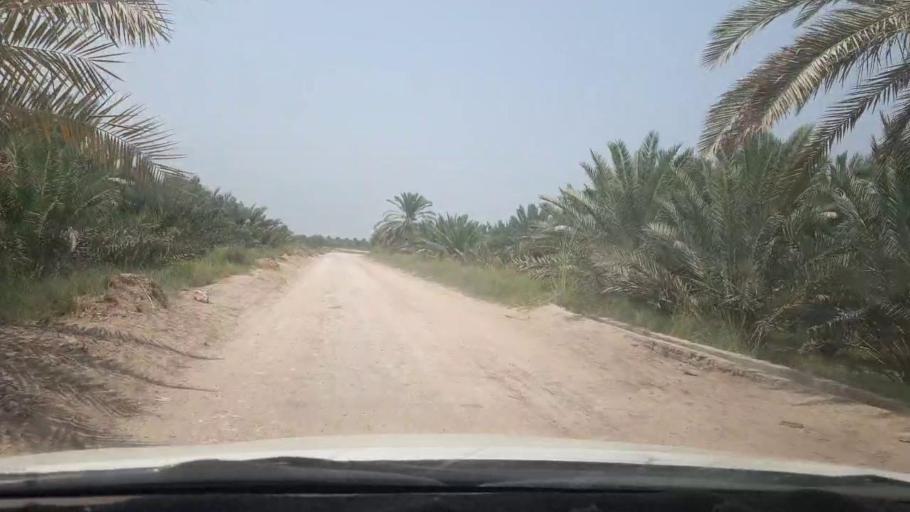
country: PK
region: Sindh
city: Khairpur
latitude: 27.5013
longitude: 68.8719
